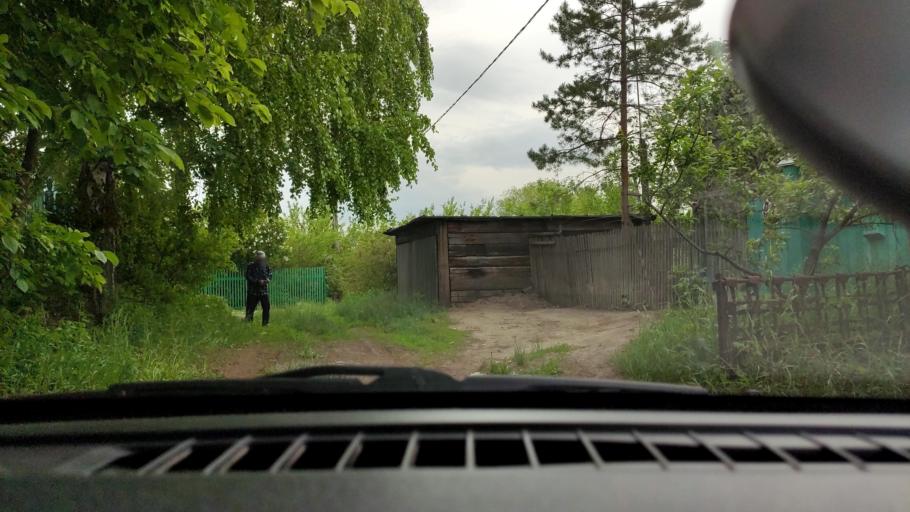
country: RU
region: Samara
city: Samara
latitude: 53.1728
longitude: 50.1665
